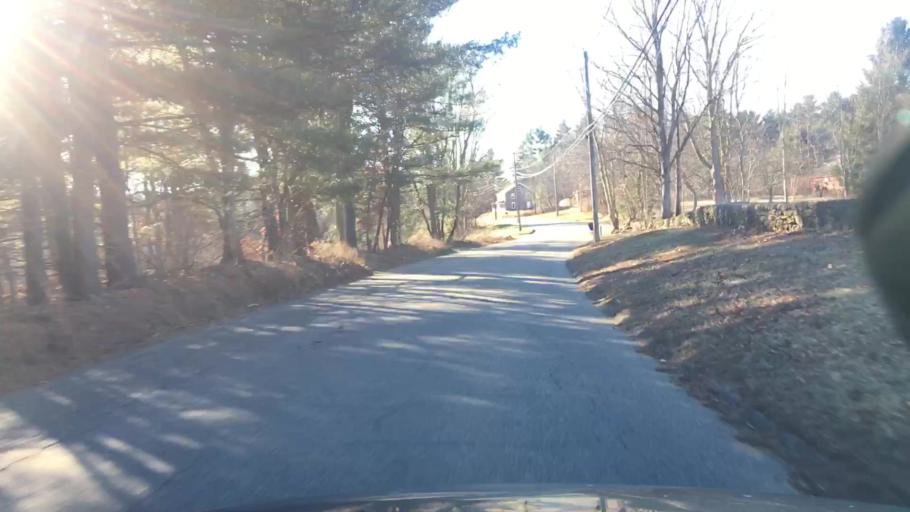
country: US
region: Connecticut
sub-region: Tolland County
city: Stafford
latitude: 41.9792
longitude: -72.2968
